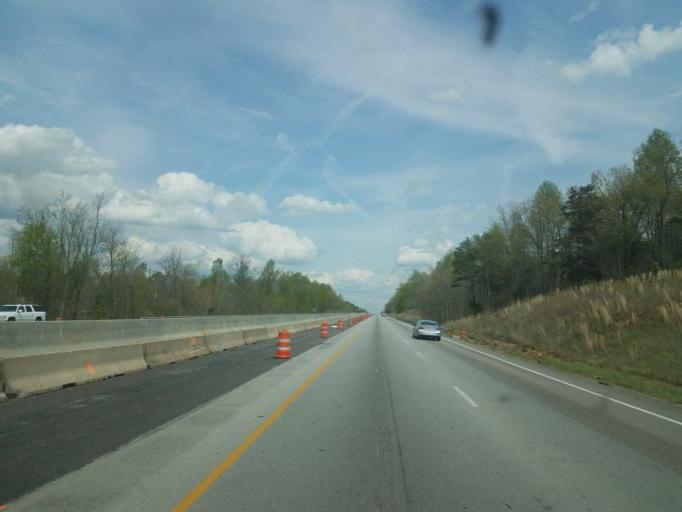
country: US
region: Kentucky
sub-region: Hardin County
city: Elizabethtown
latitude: 37.6367
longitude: -85.8598
